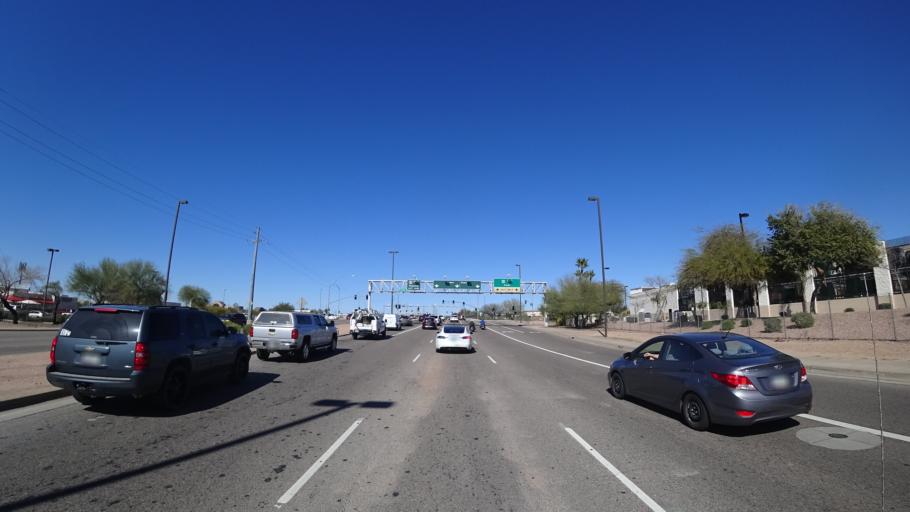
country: US
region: Arizona
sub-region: Maricopa County
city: Gilbert
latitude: 33.3849
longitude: -111.6847
